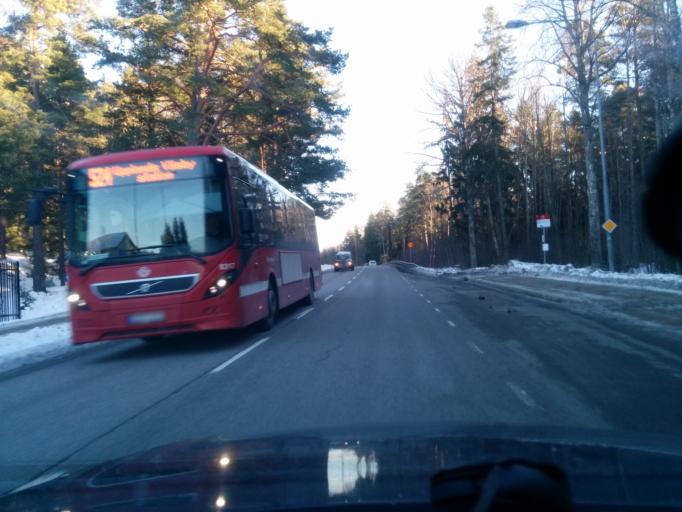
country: SE
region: Stockholm
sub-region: Taby Kommun
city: Taby
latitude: 59.4724
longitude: 18.1075
